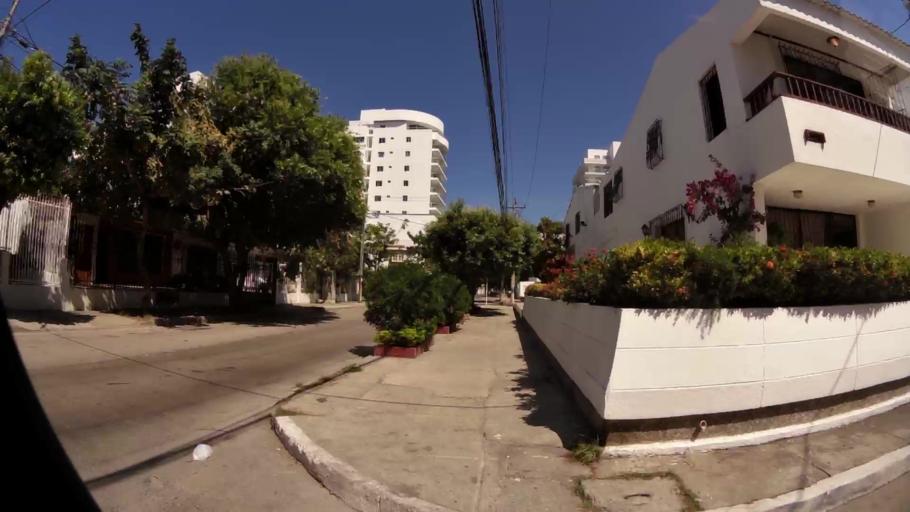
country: CO
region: Bolivar
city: Cartagena
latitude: 10.4436
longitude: -75.5217
